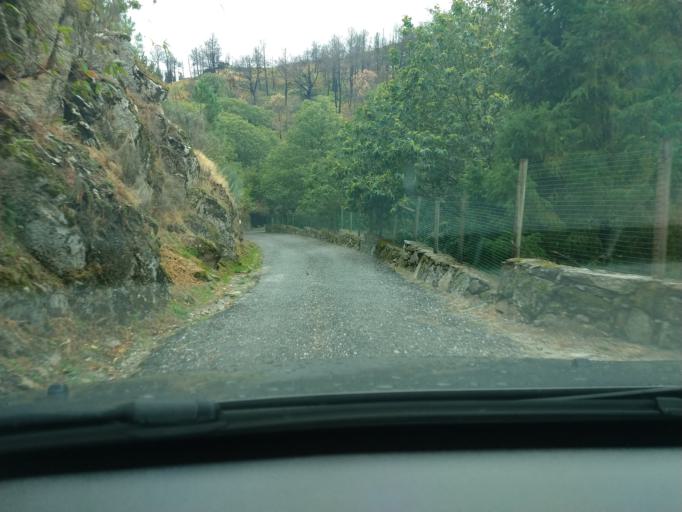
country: PT
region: Guarda
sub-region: Seia
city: Seia
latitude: 40.4191
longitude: -7.6723
